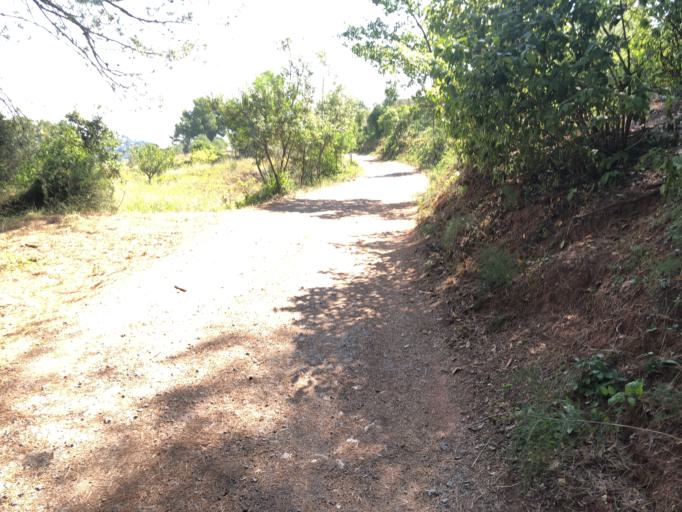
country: ES
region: Catalonia
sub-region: Provincia de Barcelona
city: Corbera de Llobregat
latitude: 41.4193
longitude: 1.9037
